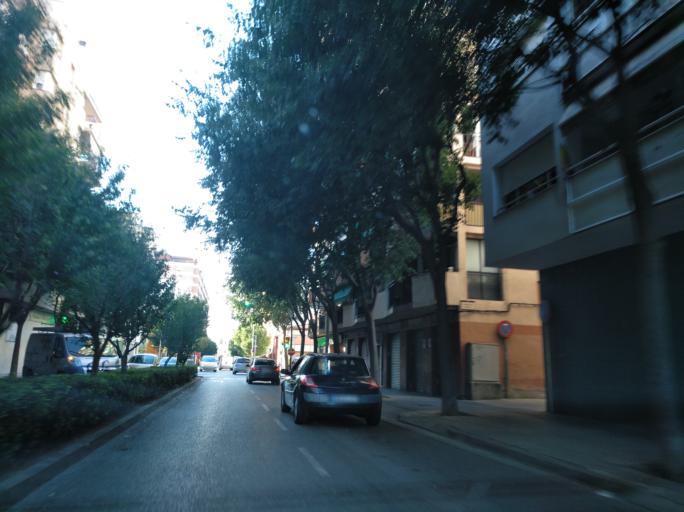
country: ES
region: Catalonia
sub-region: Provincia de Girona
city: Salt
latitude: 41.9722
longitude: 2.7922
